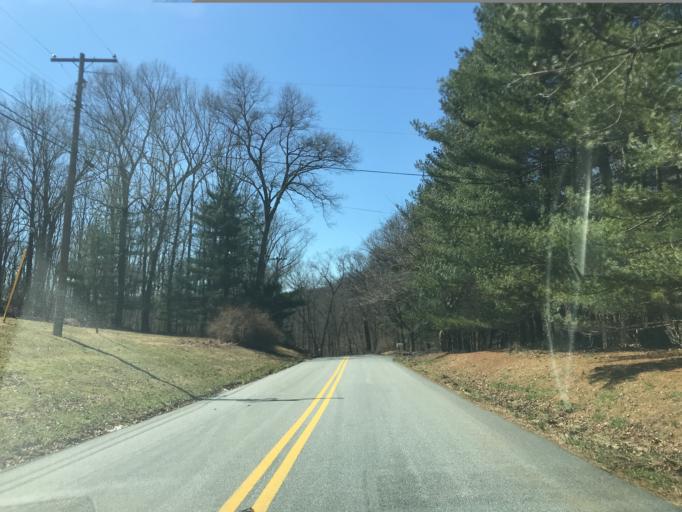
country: US
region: Pennsylvania
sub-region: York County
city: New Freedom
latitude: 39.6789
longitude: -76.6614
